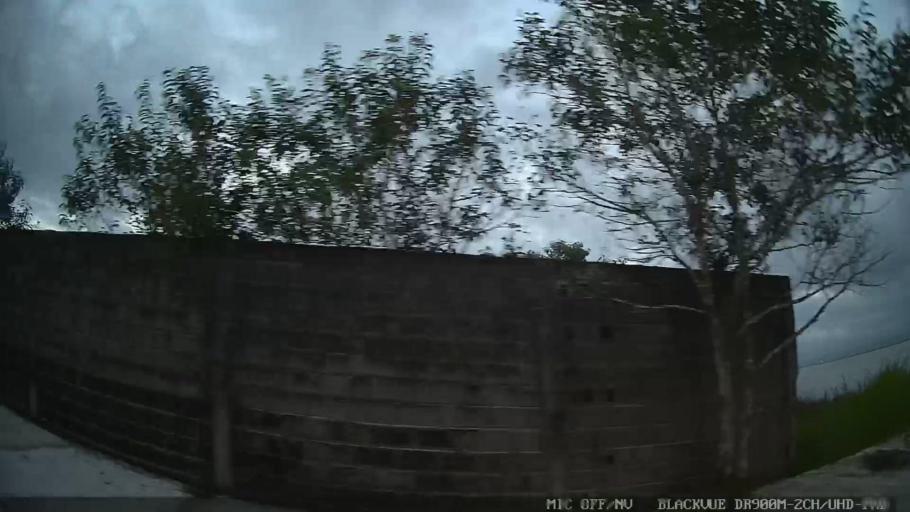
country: BR
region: Sao Paulo
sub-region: Itanhaem
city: Itanhaem
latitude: -24.1884
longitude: -46.8311
